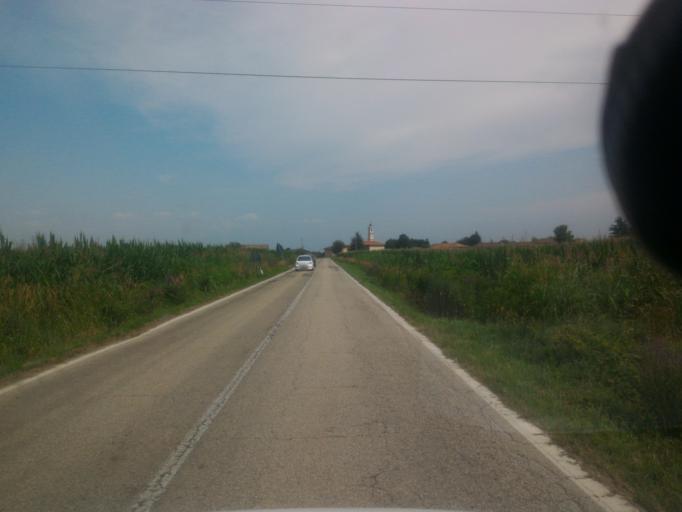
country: IT
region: Piedmont
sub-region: Provincia di Torino
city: Buriasco
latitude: 44.8555
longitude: 7.4433
